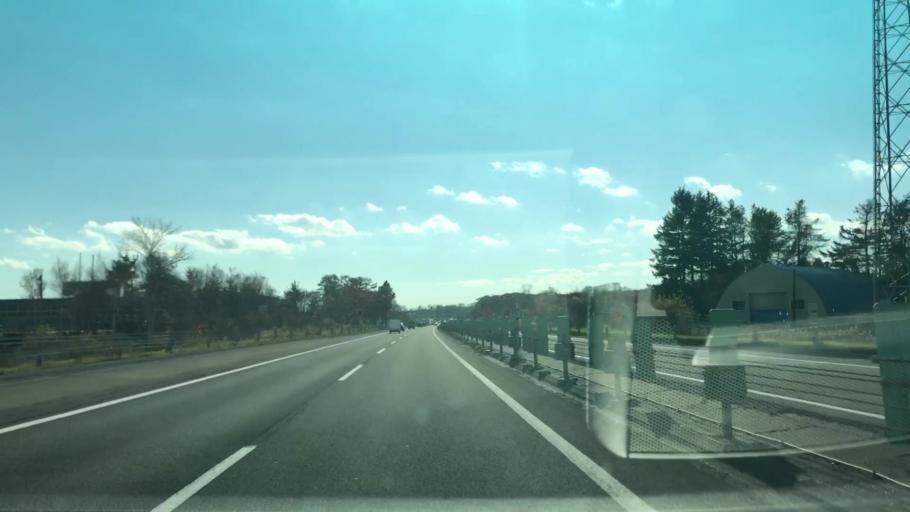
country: JP
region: Hokkaido
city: Kitahiroshima
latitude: 42.9005
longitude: 141.5506
